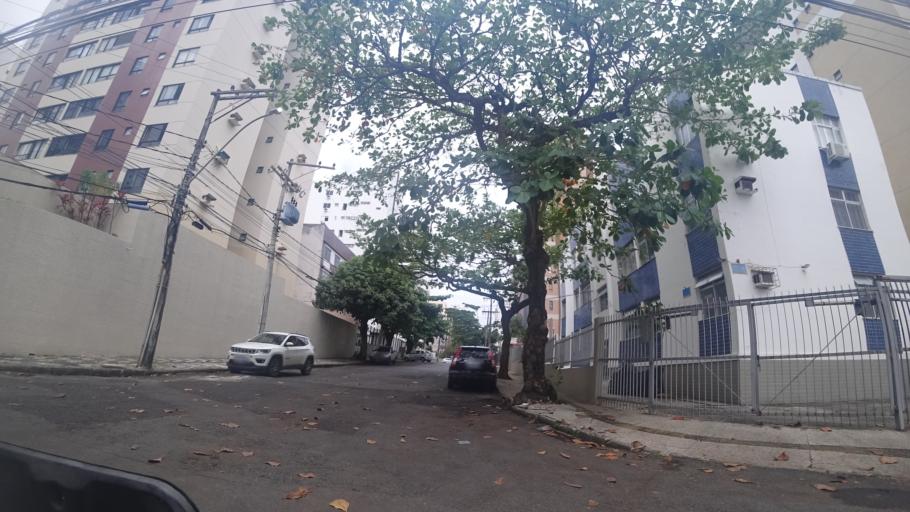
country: BR
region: Bahia
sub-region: Salvador
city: Salvador
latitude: -13.0000
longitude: -38.4562
